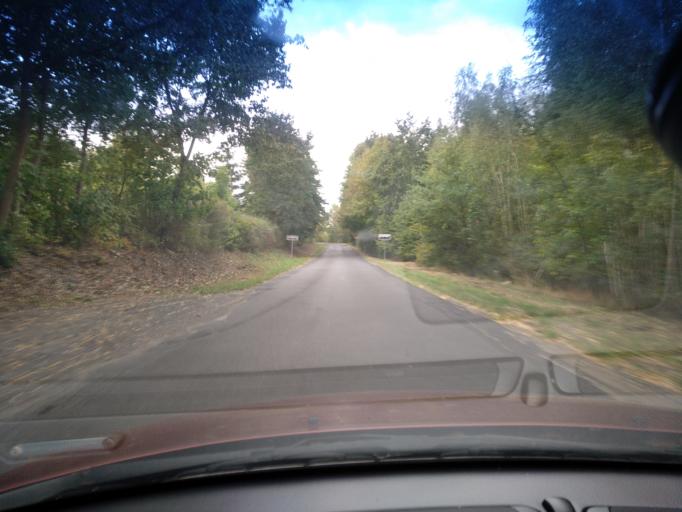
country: DE
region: Saxony
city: Goerlitz
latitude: 51.1638
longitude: 15.0006
